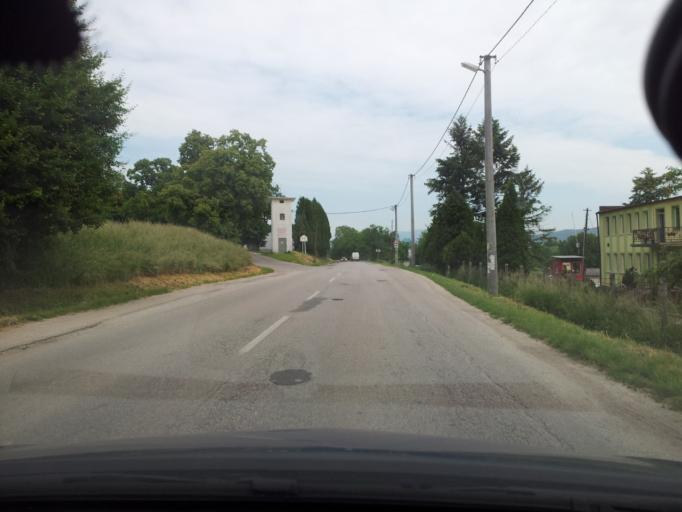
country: SK
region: Nitriansky
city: Partizanske
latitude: 48.6140
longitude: 18.4339
